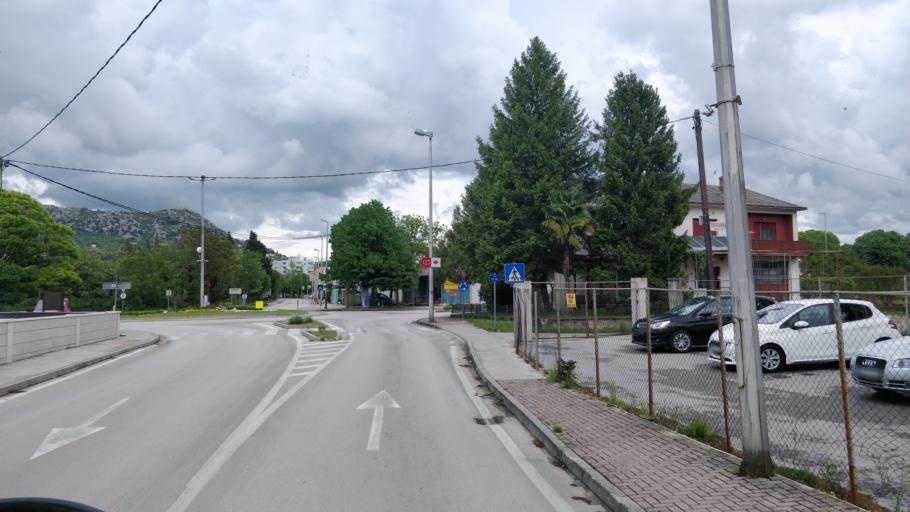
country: BA
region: Federation of Bosnia and Herzegovina
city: Ljubuski
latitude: 43.1904
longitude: 17.5341
